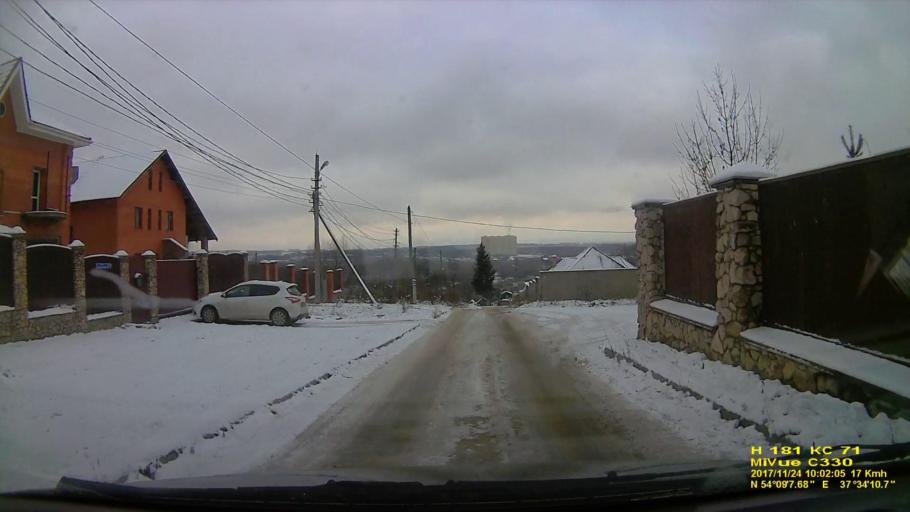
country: RU
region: Tula
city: Mendeleyevskiy
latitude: 54.1521
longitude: 37.5696
